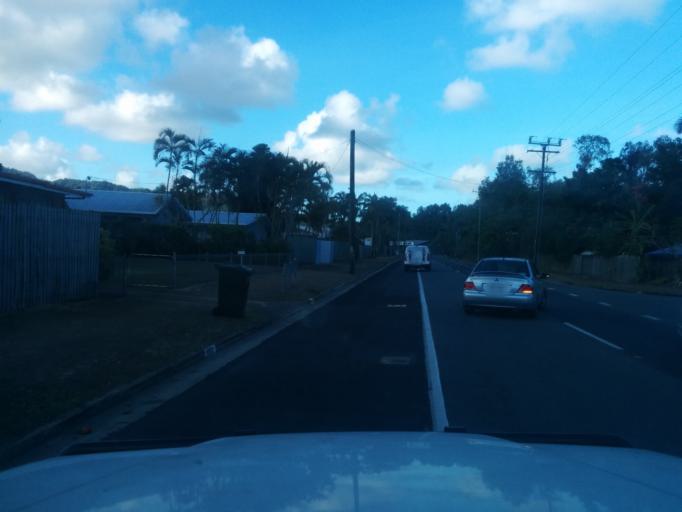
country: AU
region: Queensland
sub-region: Cairns
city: Cairns
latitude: -16.9194
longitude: 145.7469
